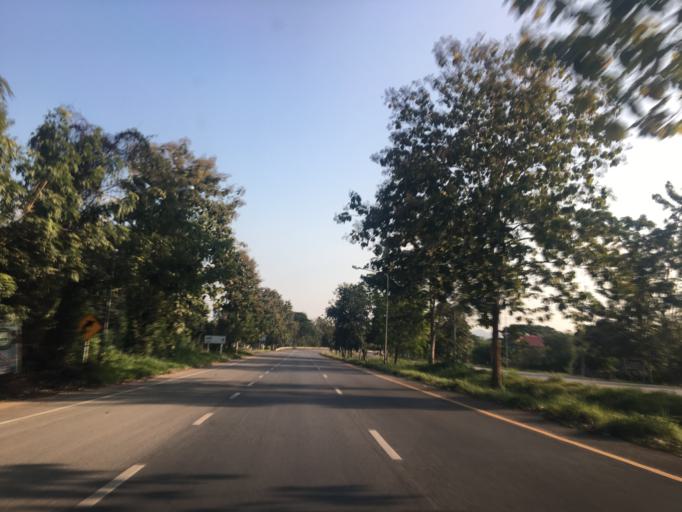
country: TH
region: Lampang
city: Ngao
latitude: 18.7664
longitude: 99.9730
